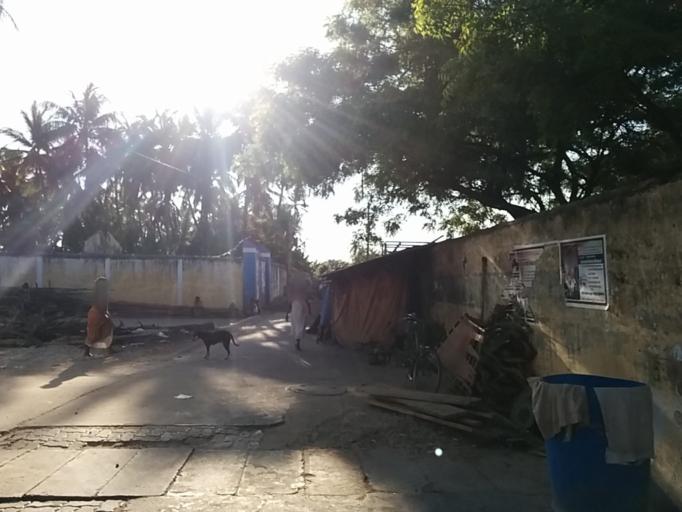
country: IN
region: Pondicherry
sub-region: Puducherry
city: Puducherry
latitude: 11.9175
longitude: 79.8305
